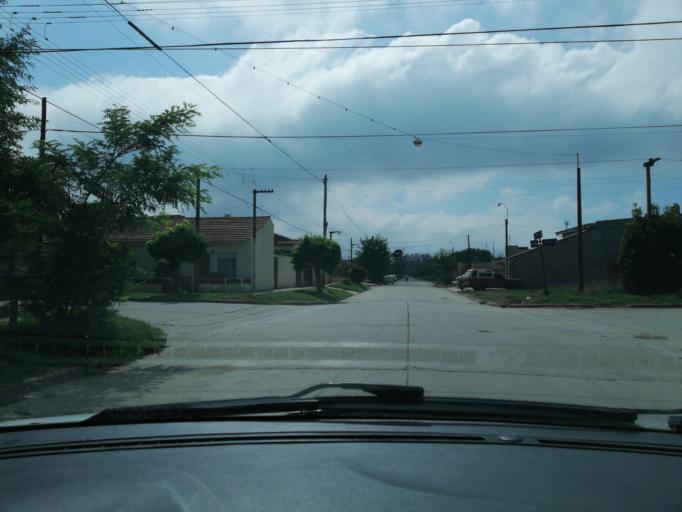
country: AR
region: Buenos Aires
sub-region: Partido de Balcarce
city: Balcarce
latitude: -37.8502
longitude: -58.2431
